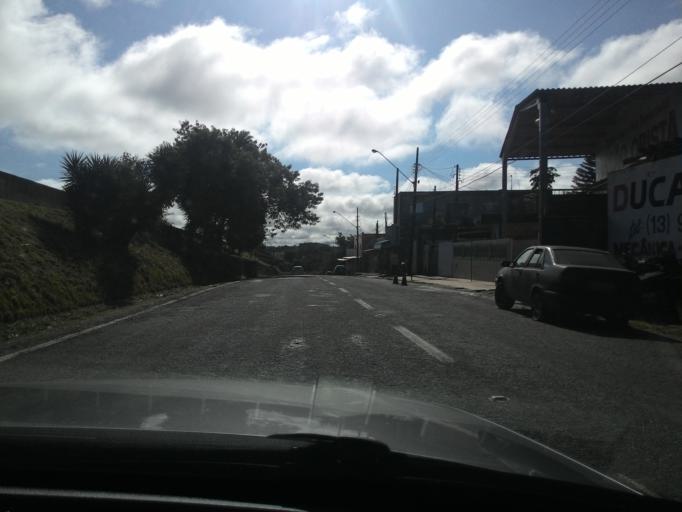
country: BR
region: Sao Paulo
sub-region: Registro
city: Registro
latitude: -24.4919
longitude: -47.8363
